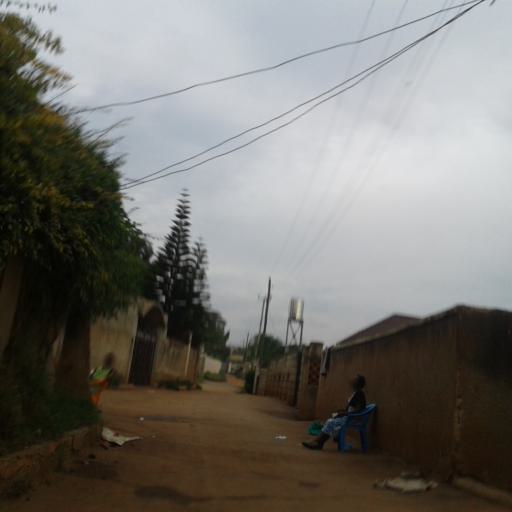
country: UG
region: Central Region
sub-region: Kampala District
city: Kampala
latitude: 0.2481
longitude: 32.6219
